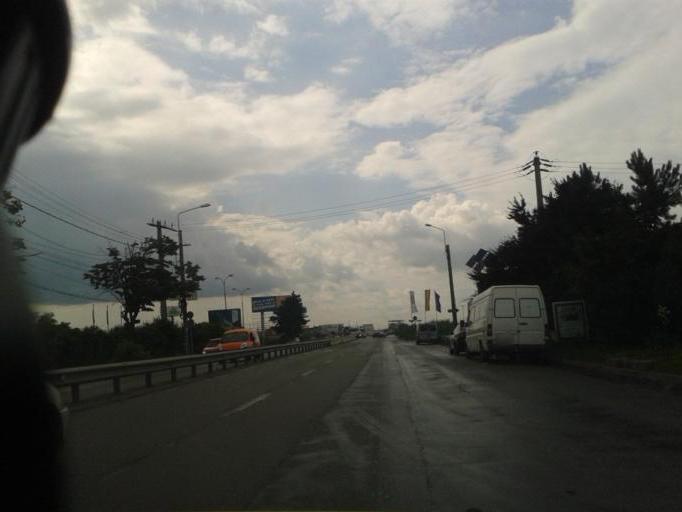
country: RO
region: Prahova
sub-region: Comuna Paulesti
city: Paulesti
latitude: 44.9636
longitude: 25.9734
